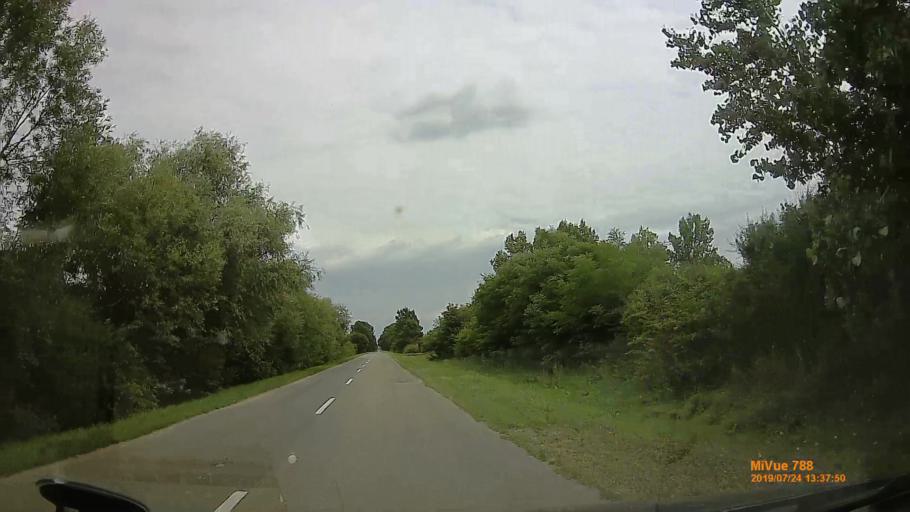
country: HU
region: Szabolcs-Szatmar-Bereg
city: Aranyosapati
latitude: 48.2290
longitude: 22.3090
